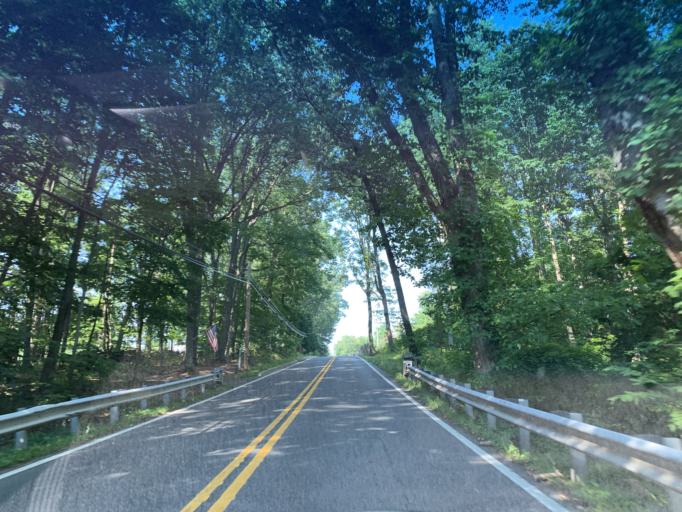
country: US
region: Maryland
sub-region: Montgomery County
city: Clarksburg
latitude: 39.2316
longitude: -77.3650
